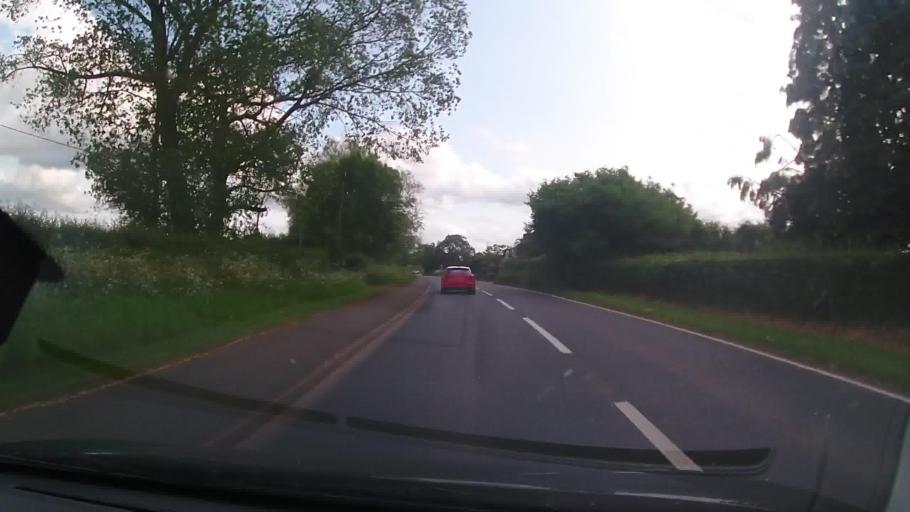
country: GB
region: England
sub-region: Shropshire
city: Clive
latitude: 52.8004
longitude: -2.7543
